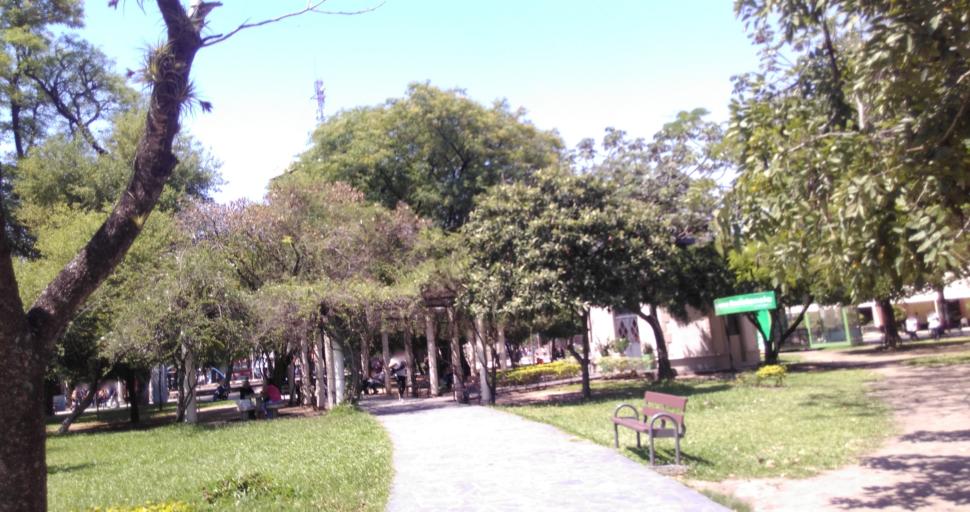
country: AR
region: Chaco
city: Resistencia
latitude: -27.4511
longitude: -58.9873
